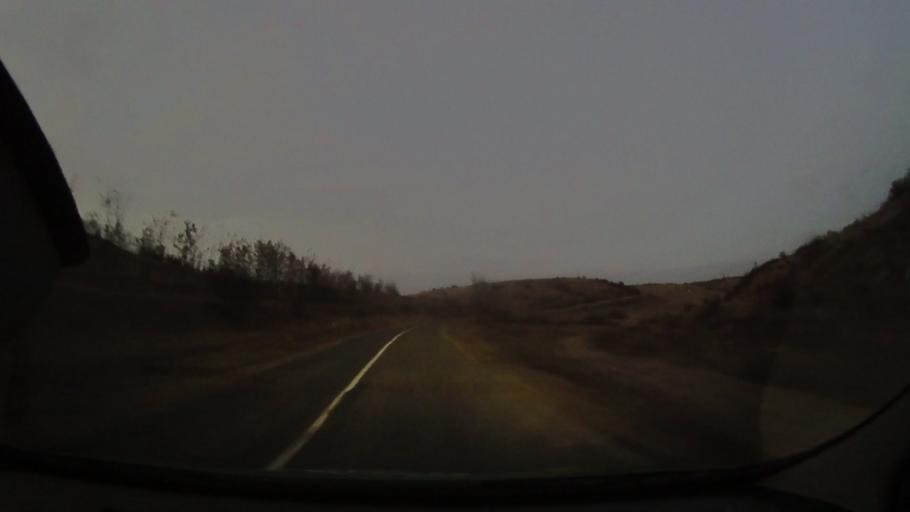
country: RO
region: Constanta
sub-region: Comuna Ion Corvin
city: Ion Corvin
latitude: 44.1188
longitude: 27.8113
